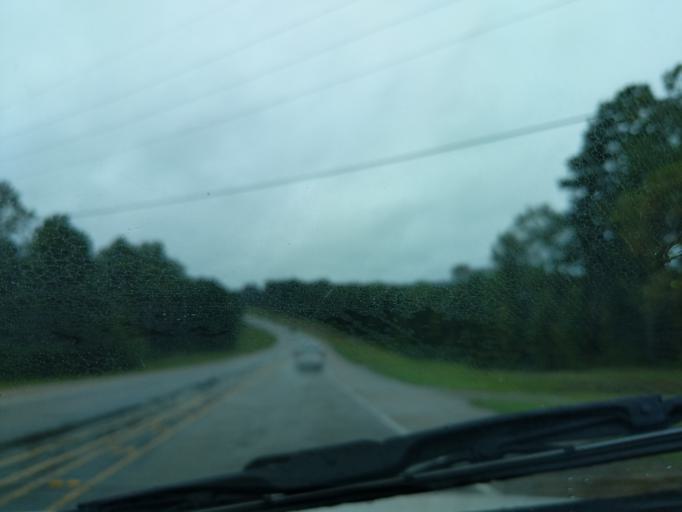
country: US
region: Louisiana
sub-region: Webster Parish
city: Minden
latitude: 32.5995
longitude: -93.2498
